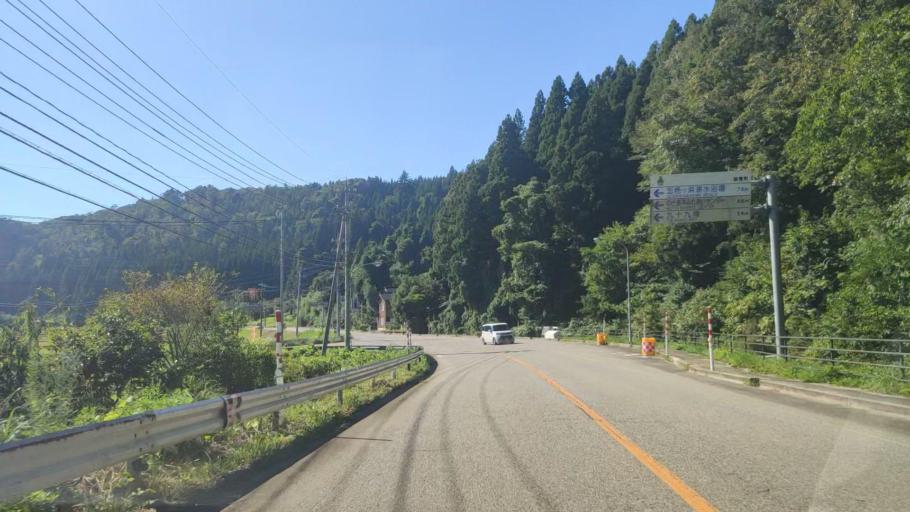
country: JP
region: Ishikawa
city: Nanao
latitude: 37.3405
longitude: 137.2220
